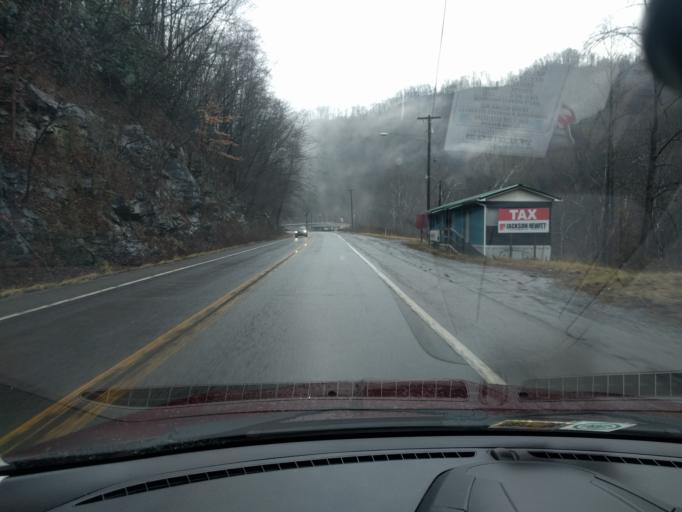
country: US
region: West Virginia
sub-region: McDowell County
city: Welch
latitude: 37.4302
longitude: -81.5612
